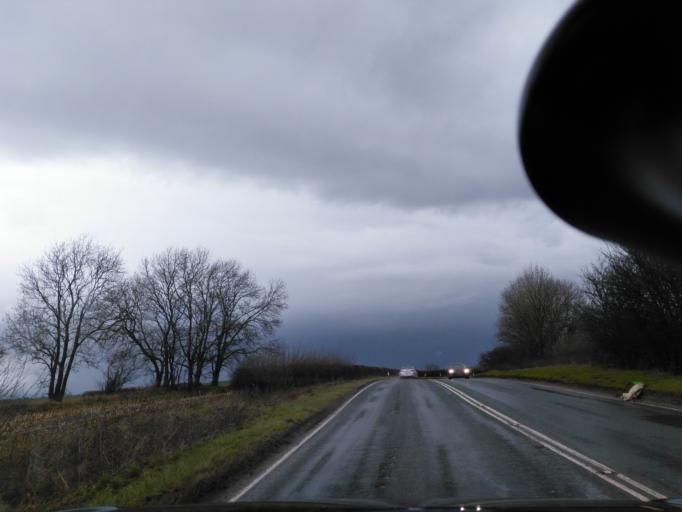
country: GB
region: England
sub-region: North Yorkshire
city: Ripon
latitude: 54.0930
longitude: -1.5303
